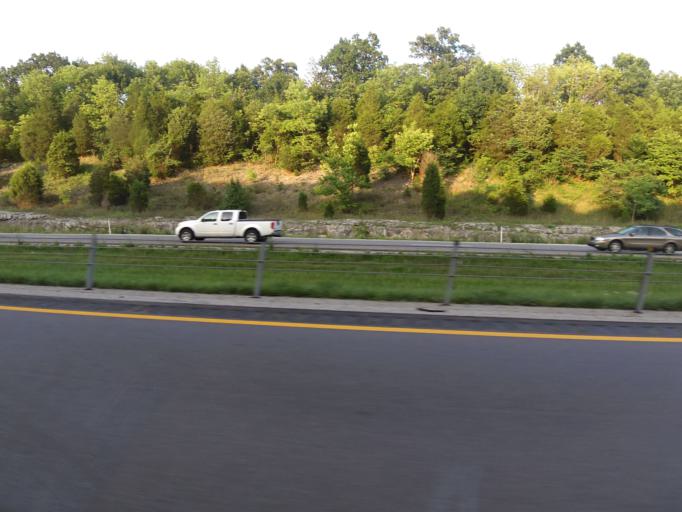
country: US
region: Kentucky
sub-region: Rockcastle County
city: Mount Vernon
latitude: 37.4039
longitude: -84.3392
